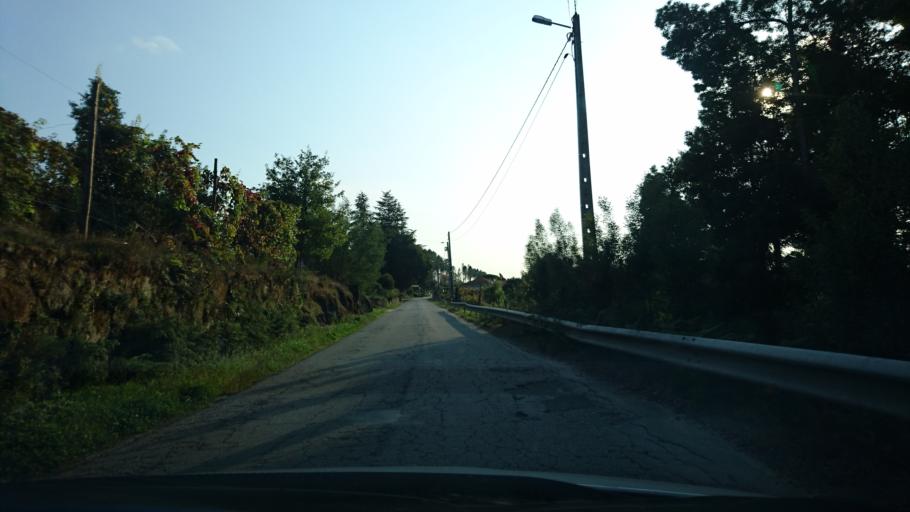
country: PT
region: Vila Real
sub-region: Mondim de Basto
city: Mondim de Basto
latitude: 41.4286
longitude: -7.9335
